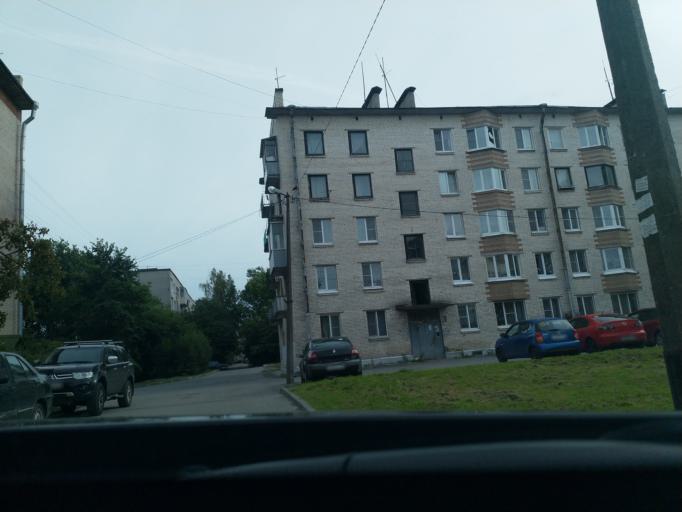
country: RU
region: Leningrad
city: Nikol'skoye
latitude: 59.7037
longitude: 30.7901
